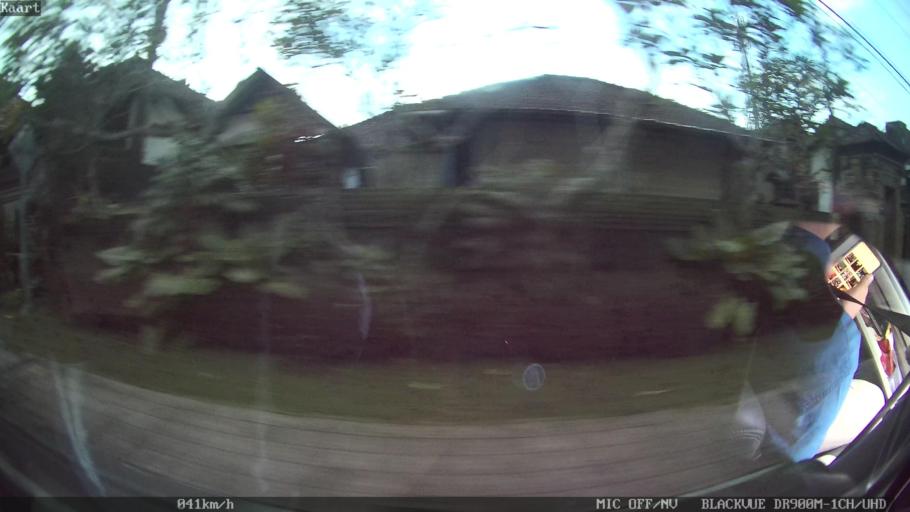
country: ID
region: Bali
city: Bunutan
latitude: -8.4740
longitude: 115.2496
